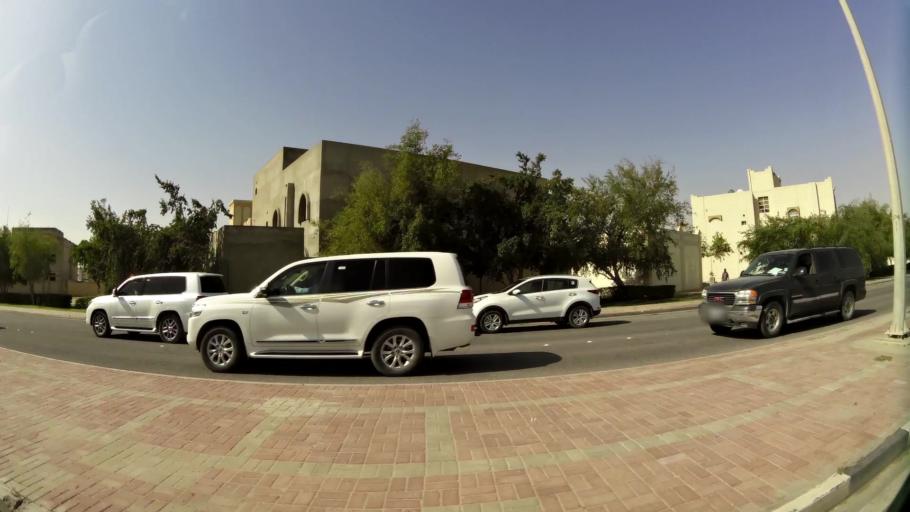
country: QA
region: Baladiyat ad Dawhah
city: Doha
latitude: 25.3422
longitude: 51.5099
